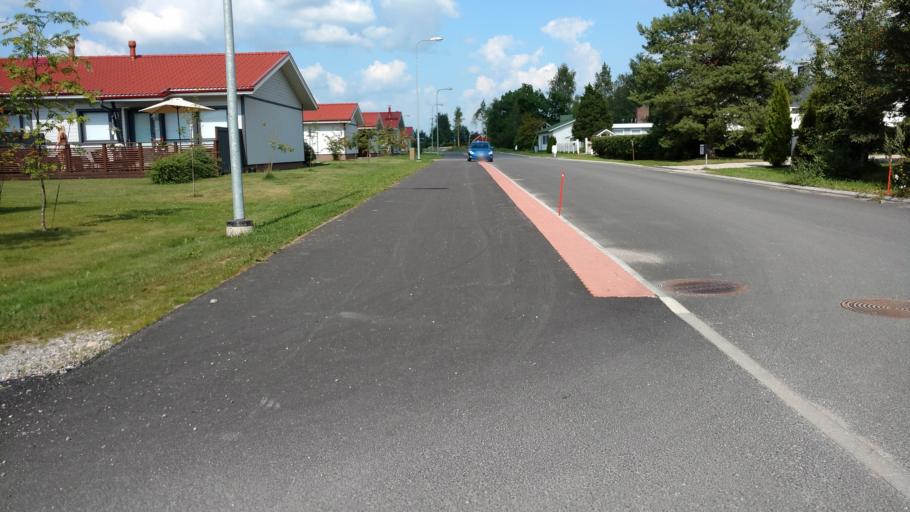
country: FI
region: Varsinais-Suomi
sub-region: Salo
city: Salo
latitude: 60.4032
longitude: 23.1651
